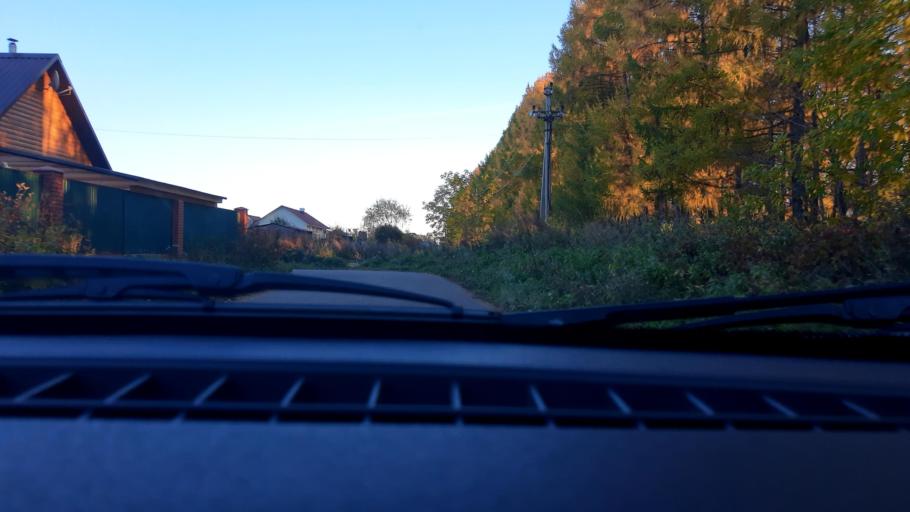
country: RU
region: Bashkortostan
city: Ufa
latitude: 54.8548
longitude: 56.0103
